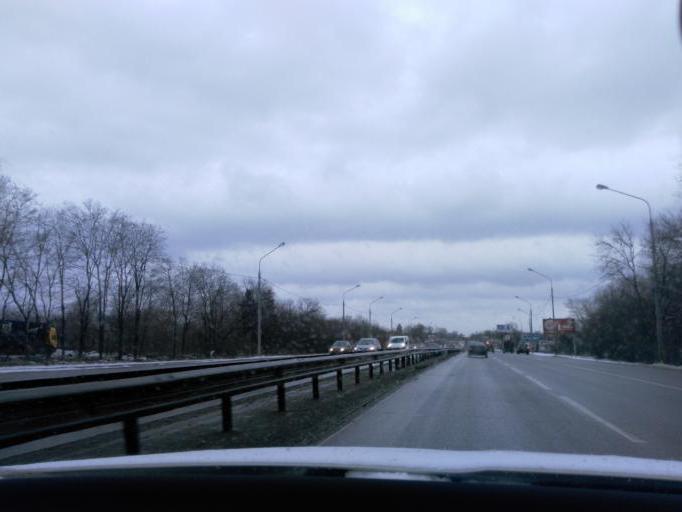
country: RU
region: Moskovskaya
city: Novopodrezkovo
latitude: 55.9431
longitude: 37.3611
